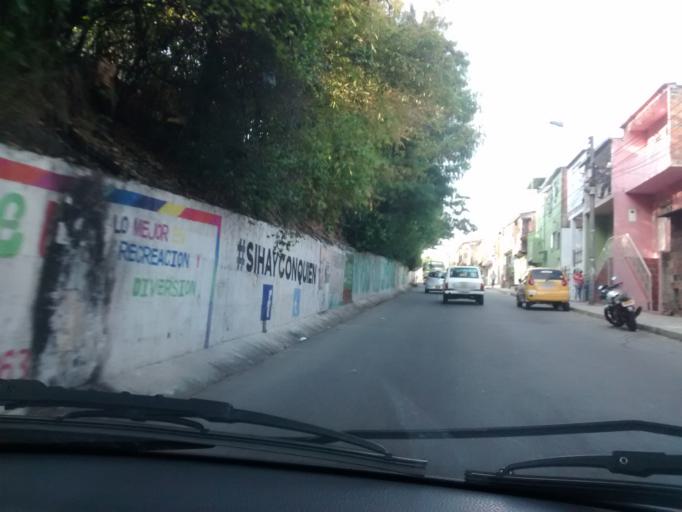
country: CO
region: Santander
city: Bucaramanga
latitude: 7.0956
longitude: -73.1251
